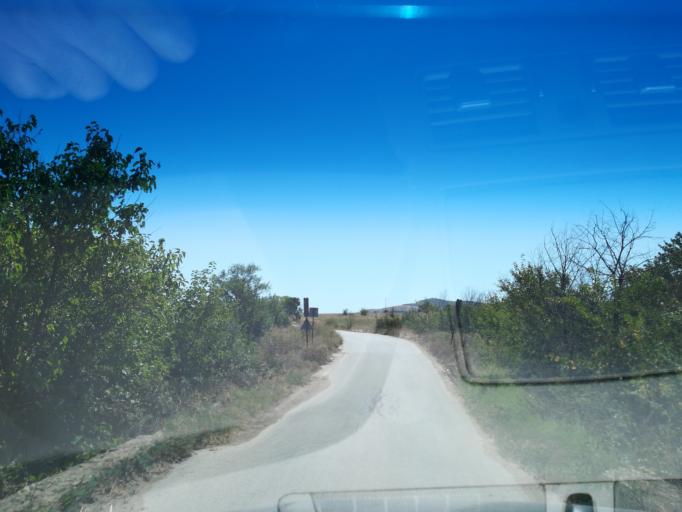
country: BG
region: Pazardzhik
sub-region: Obshtina Pazardzhik
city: Pazardzhik
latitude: 42.3524
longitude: 24.3998
